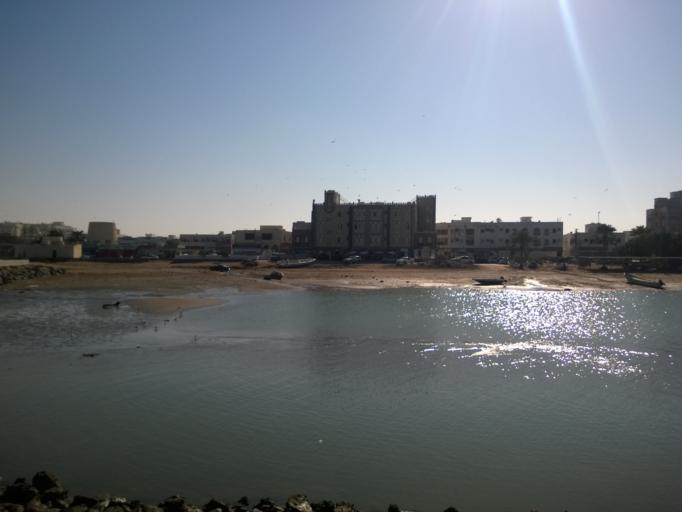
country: OM
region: Muhafazat Masqat
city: As Sib al Jadidah
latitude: 23.6871
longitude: 58.1832
